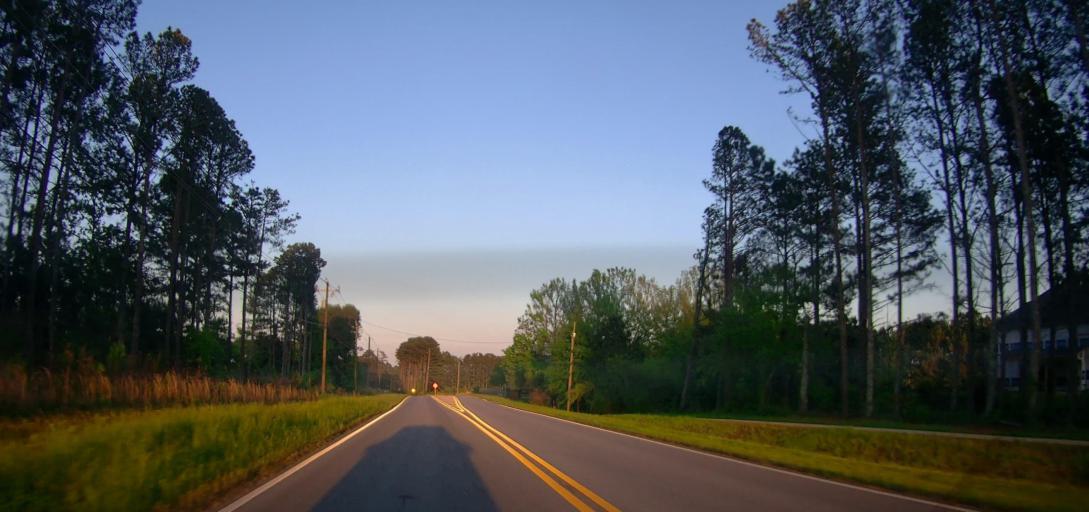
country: US
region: Georgia
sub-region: Henry County
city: McDonough
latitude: 33.4031
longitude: -84.1233
